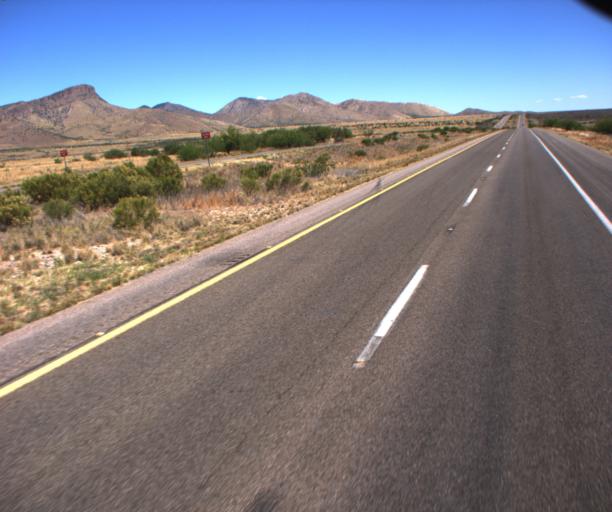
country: US
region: Arizona
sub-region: Cochise County
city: Huachuca City
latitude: 31.7827
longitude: -110.3499
